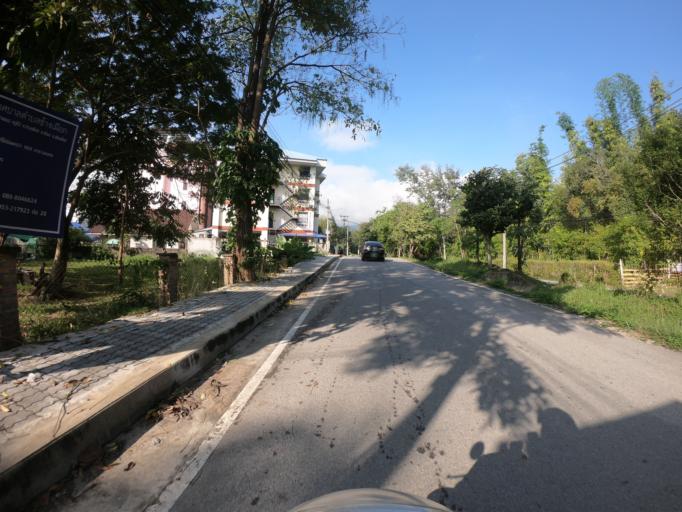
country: TH
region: Chiang Mai
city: Chiang Mai
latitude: 18.8142
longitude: 98.9667
